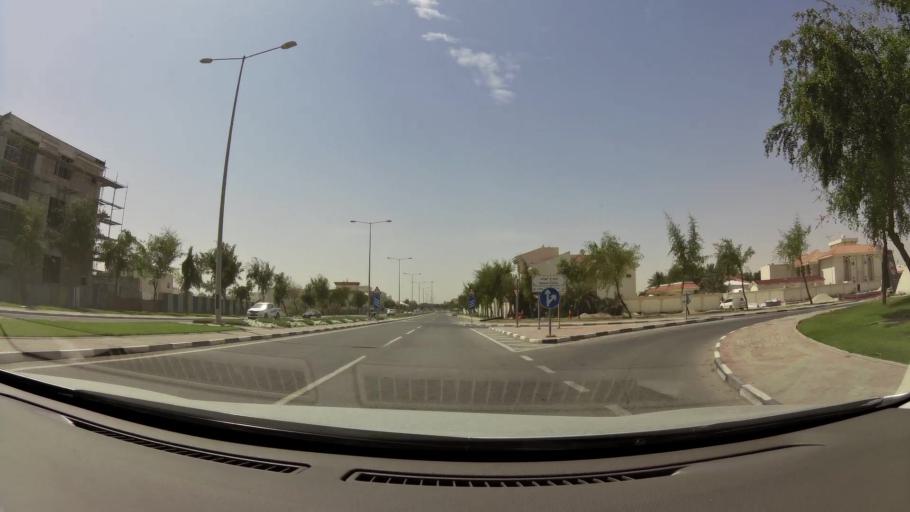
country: QA
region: Baladiyat ar Rayyan
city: Ar Rayyan
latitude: 25.2556
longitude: 51.4299
